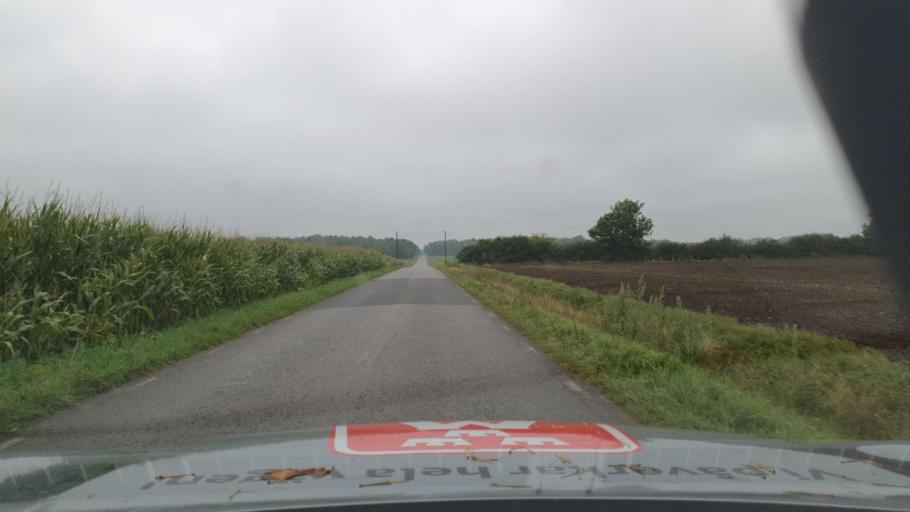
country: SE
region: Gotland
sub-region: Gotland
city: Visby
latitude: 57.7902
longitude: 18.5270
